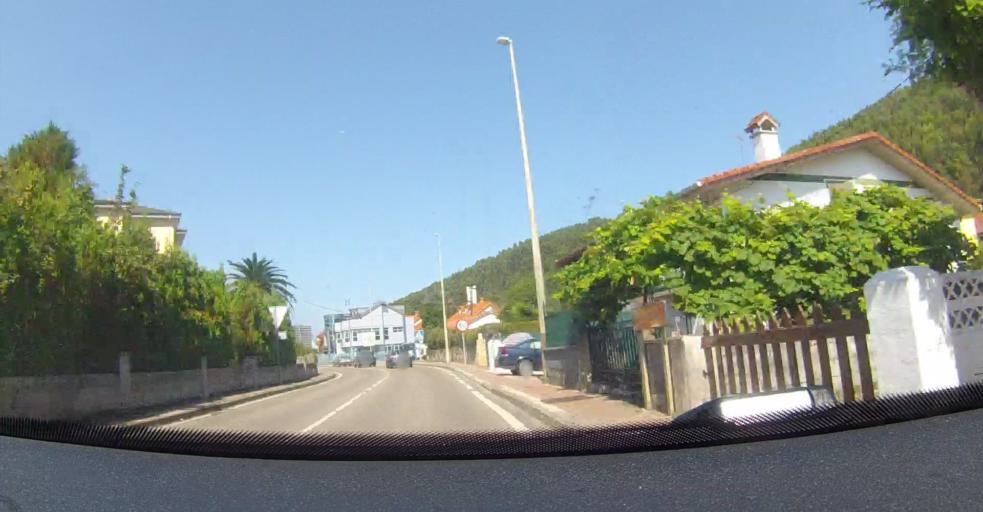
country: ES
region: Cantabria
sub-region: Provincia de Cantabria
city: Argonos
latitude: 43.4575
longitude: -3.4870
